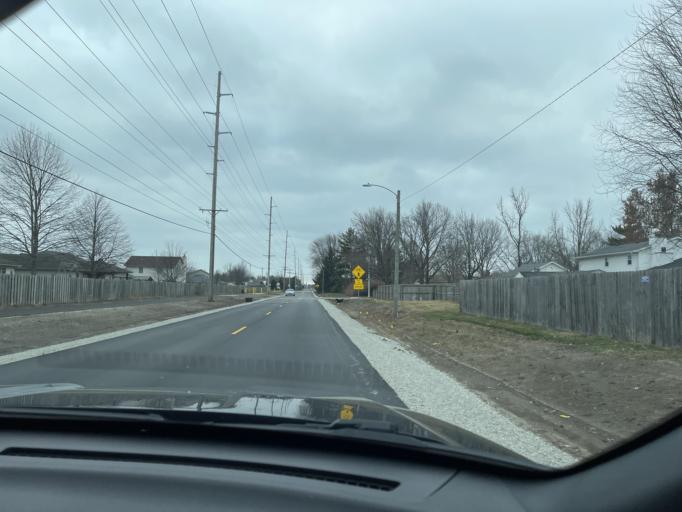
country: US
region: Illinois
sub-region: Sangamon County
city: Rochester
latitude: 39.7645
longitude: -89.5787
